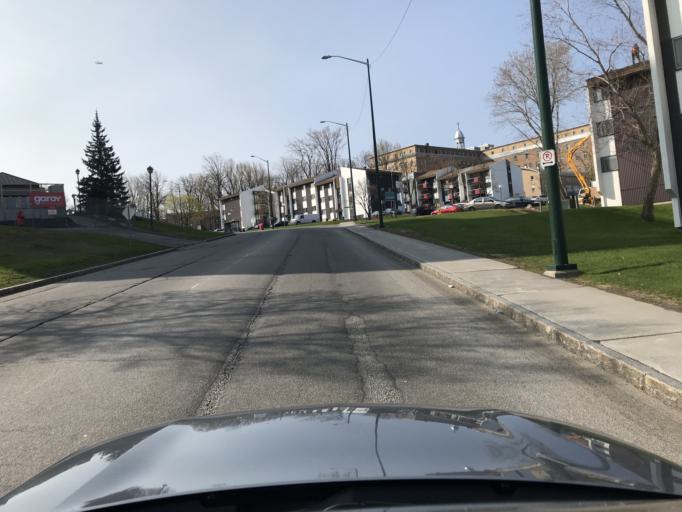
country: CA
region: Quebec
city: L'Ancienne-Lorette
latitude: 46.7909
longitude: -71.2835
